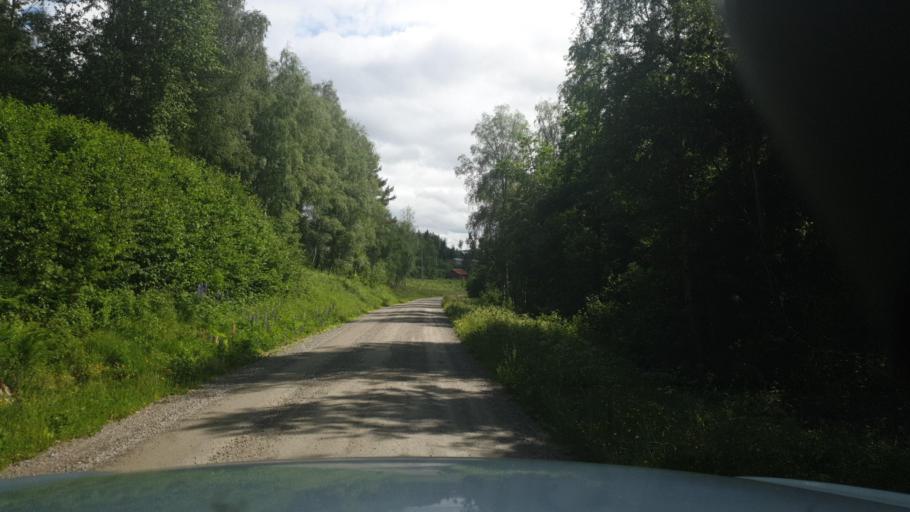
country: NO
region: Ostfold
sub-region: Romskog
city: Romskog
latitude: 59.6818
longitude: 11.9320
